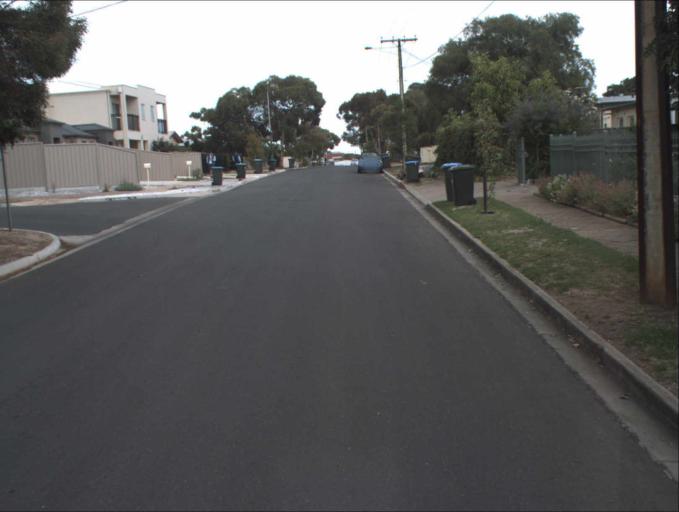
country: AU
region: South Australia
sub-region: Port Adelaide Enfield
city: Gilles Plains
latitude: -34.8464
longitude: 138.6589
